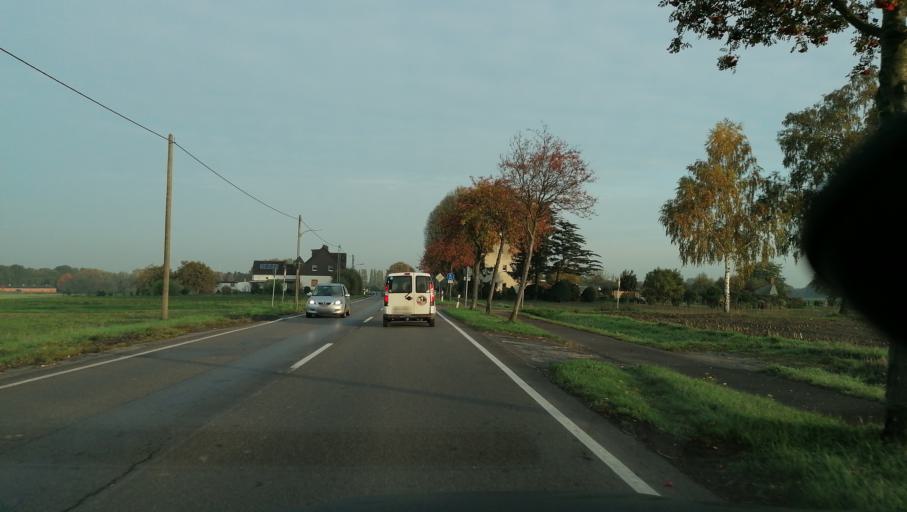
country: DE
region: North Rhine-Westphalia
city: Herten
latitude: 51.6220
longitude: 7.1602
